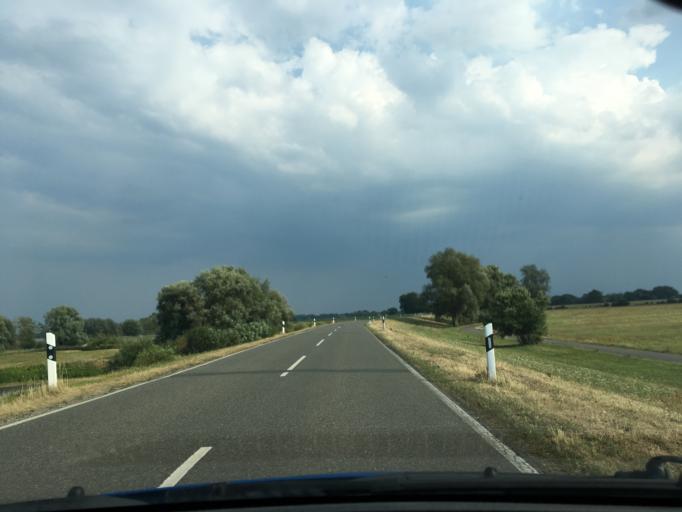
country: DE
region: Lower Saxony
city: Hitzacker
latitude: 53.1459
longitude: 11.0623
